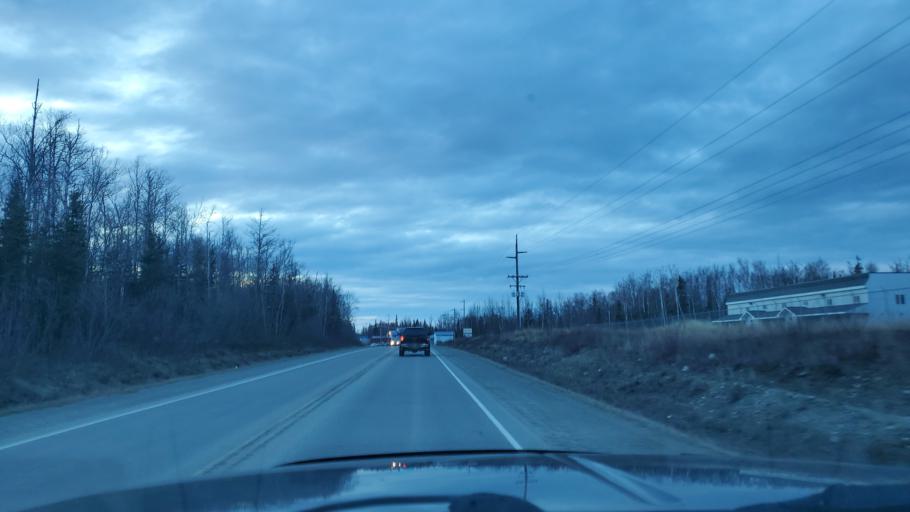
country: US
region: Alaska
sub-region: Matanuska-Susitna Borough
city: Tanaina
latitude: 61.5937
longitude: -149.3856
